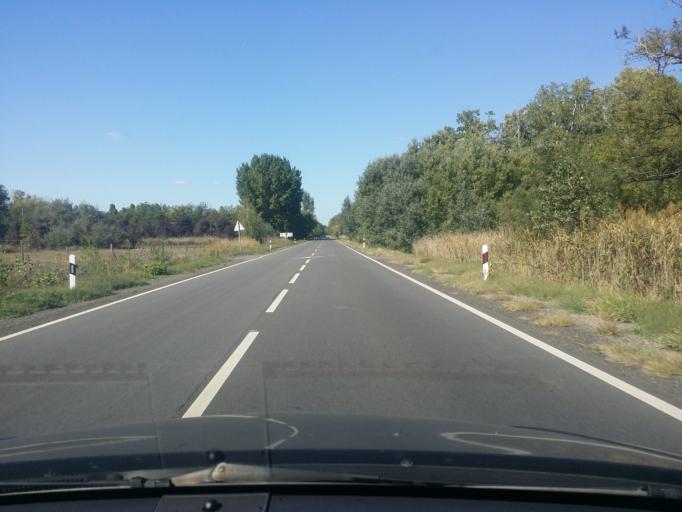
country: HU
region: Bacs-Kiskun
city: Palmonostora
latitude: 46.6388
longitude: 19.8885
